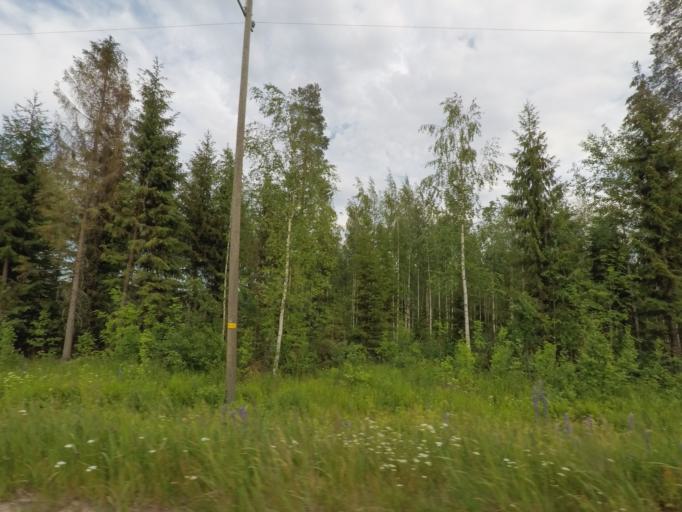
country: FI
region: Paijanne Tavastia
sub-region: Lahti
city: Lahti
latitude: 60.9213
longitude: 25.5740
